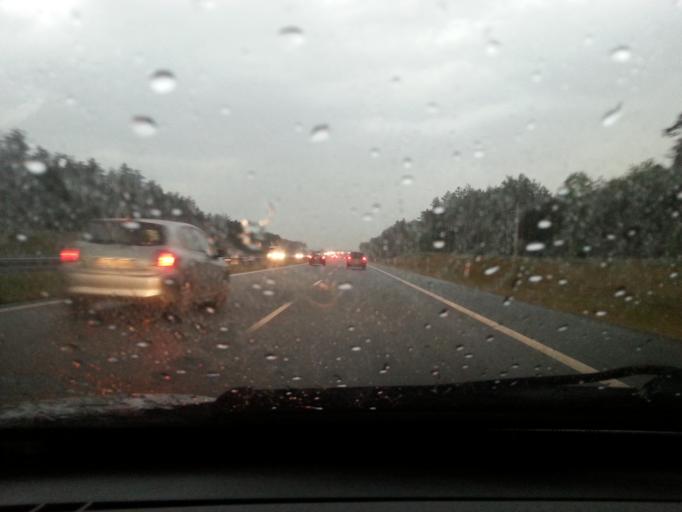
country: PL
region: Lodz Voivodeship
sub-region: powiat Lowicki
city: Lyszkowice
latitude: 51.9580
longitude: 19.8474
